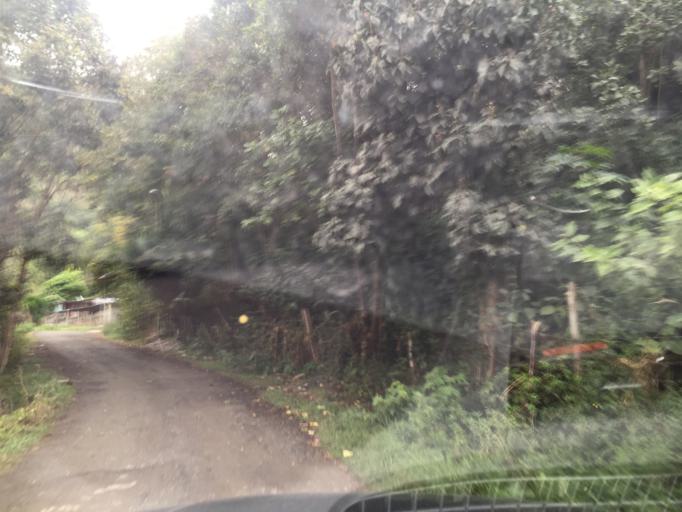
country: CO
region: Tolima
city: Cajamarca
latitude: 4.3965
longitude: -75.4467
